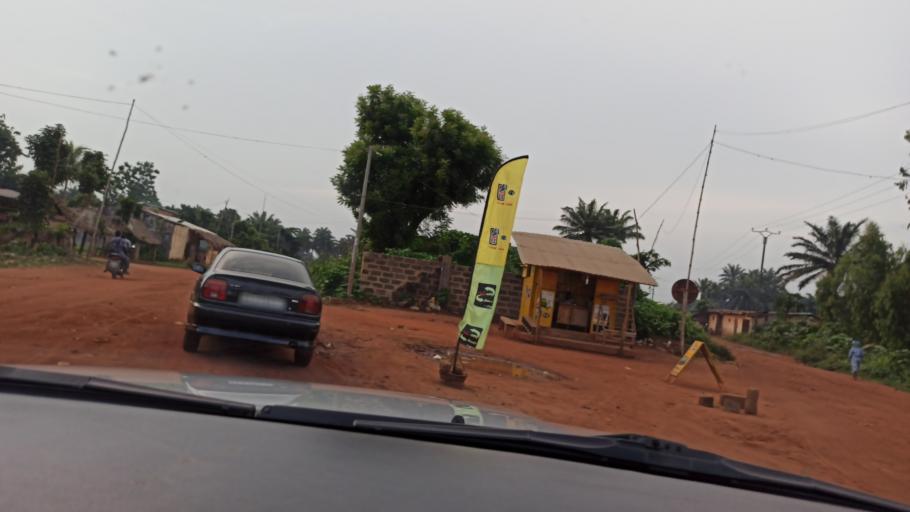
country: BJ
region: Queme
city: Porto-Novo
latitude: 6.5339
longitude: 2.6585
